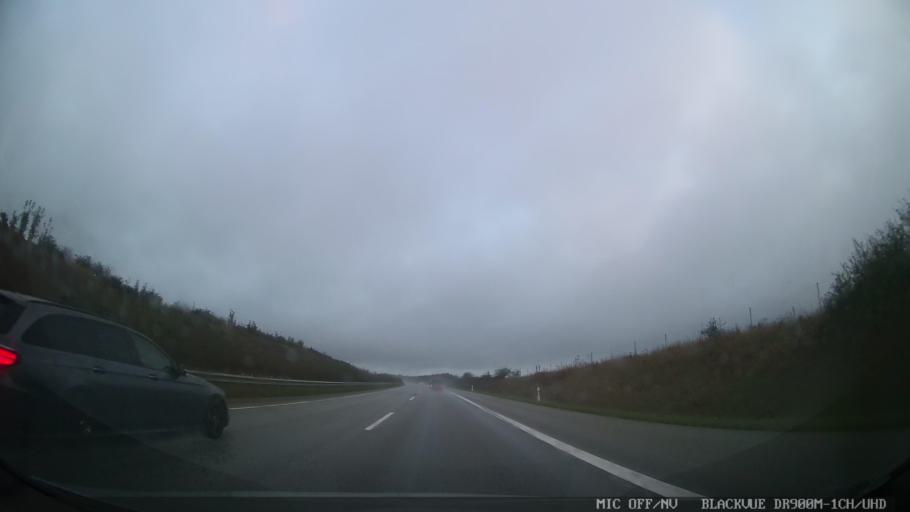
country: DE
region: Schleswig-Holstein
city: Badendorf
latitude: 53.8719
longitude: 10.5590
